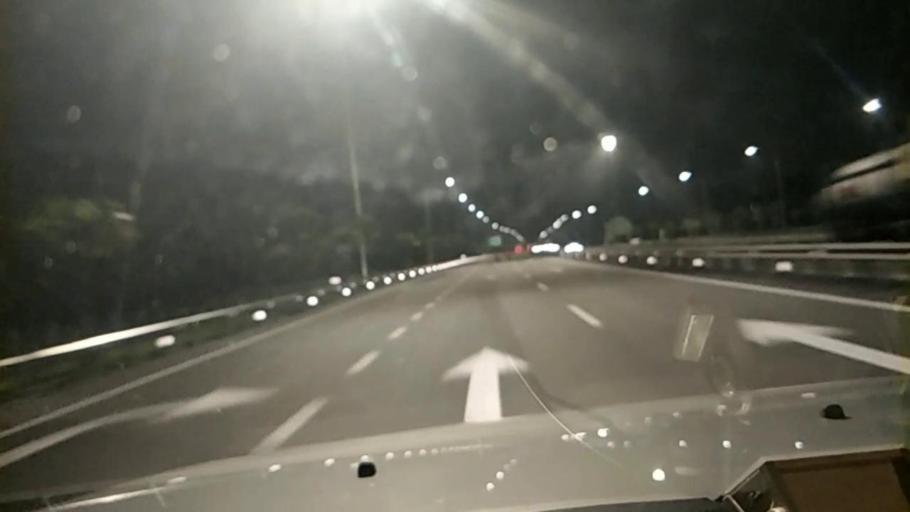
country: MY
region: Perak
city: Bagan Serai
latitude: 5.0678
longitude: 100.5909
